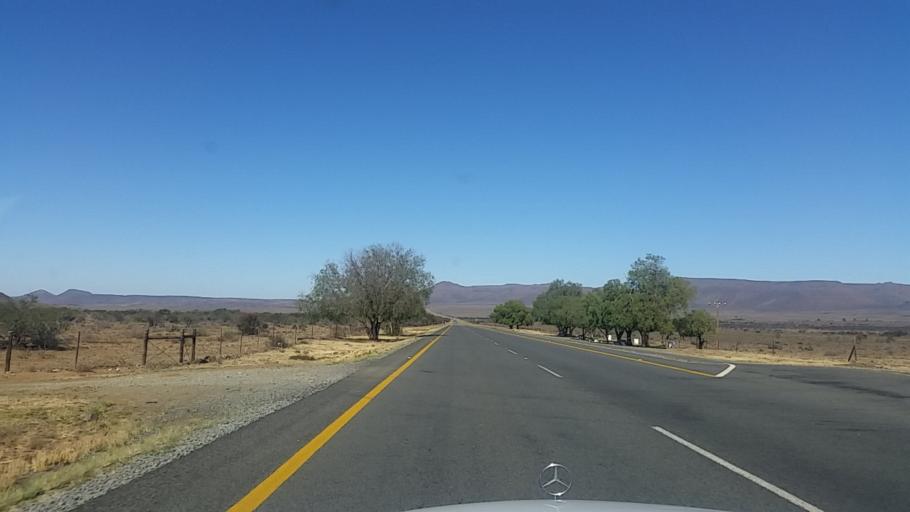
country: ZA
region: Eastern Cape
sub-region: Cacadu District Municipality
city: Graaff-Reinet
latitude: -31.9872
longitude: 24.6895
